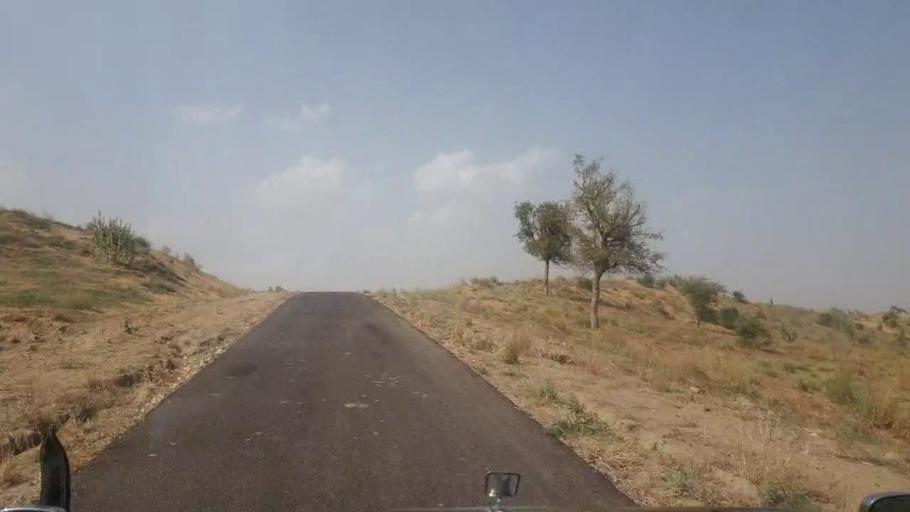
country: PK
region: Sindh
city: Islamkot
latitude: 25.1932
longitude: 70.2851
